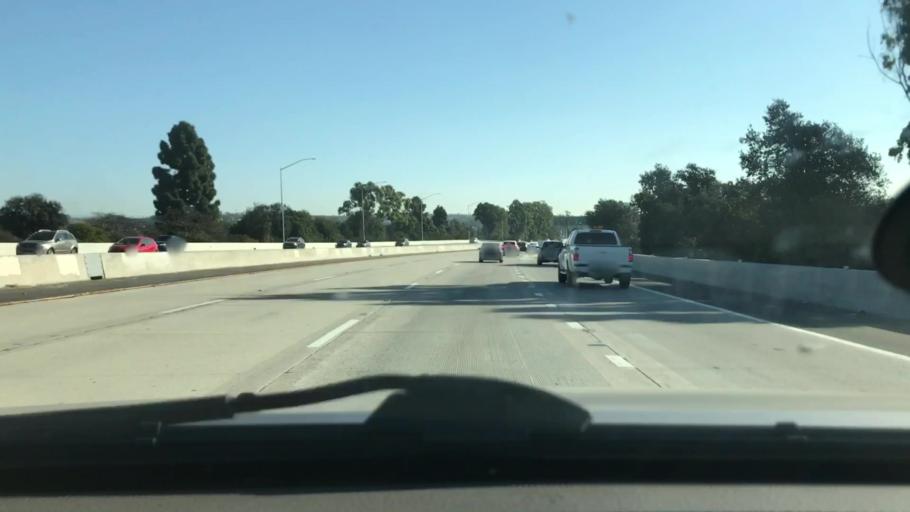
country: US
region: California
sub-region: Los Angeles County
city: Ladera Heights
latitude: 33.9881
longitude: -118.4081
